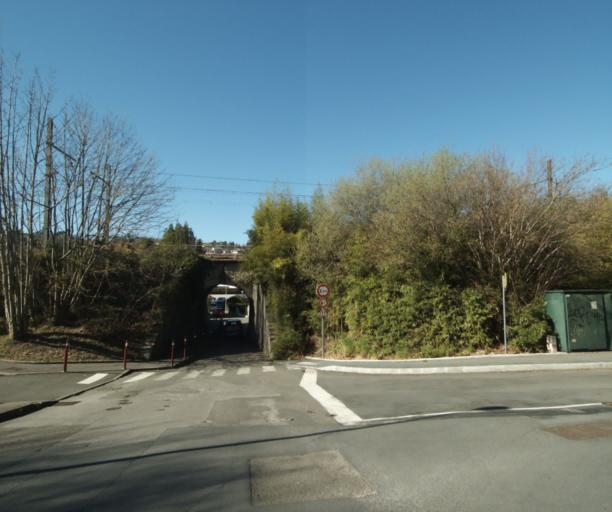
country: FR
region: Aquitaine
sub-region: Departement des Pyrenees-Atlantiques
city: Ciboure
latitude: 43.3779
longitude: -1.6699
